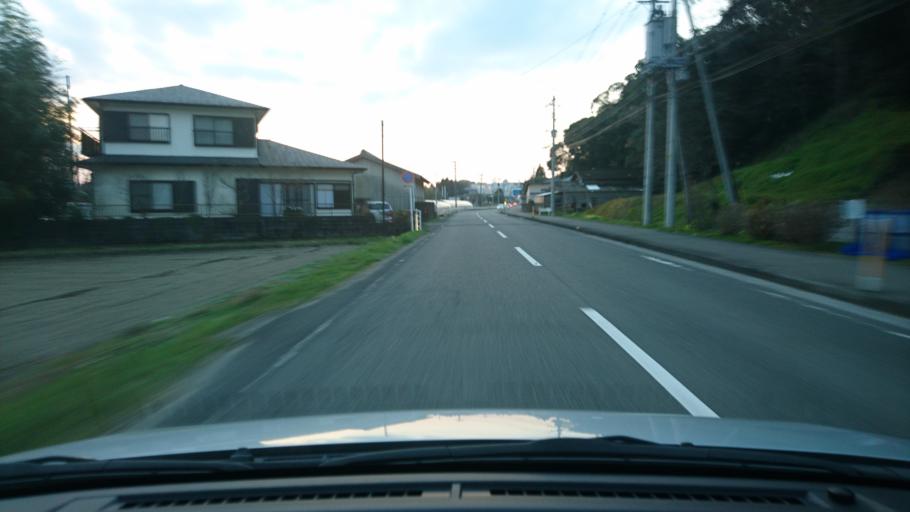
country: JP
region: Miyazaki
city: Miyazaki-shi
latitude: 31.8538
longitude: 131.4127
